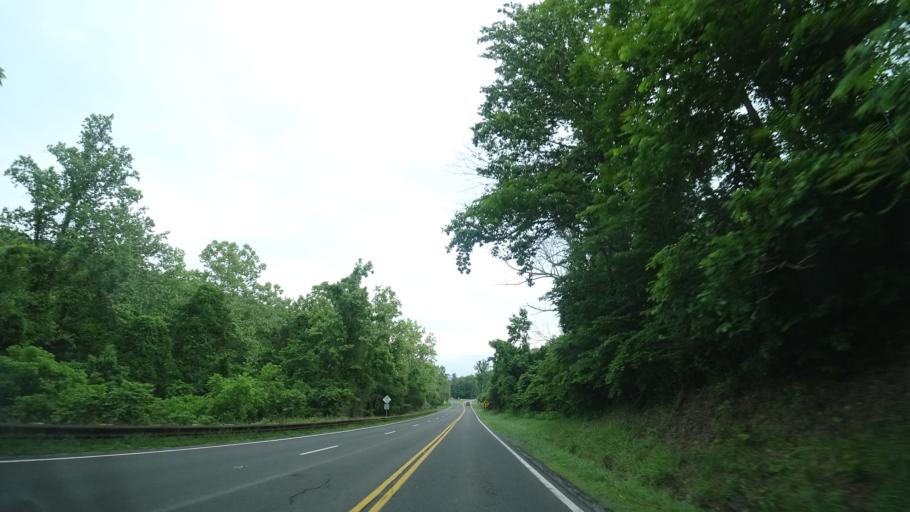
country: US
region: Virginia
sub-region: Page County
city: Luray
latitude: 38.6594
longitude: -78.3706
